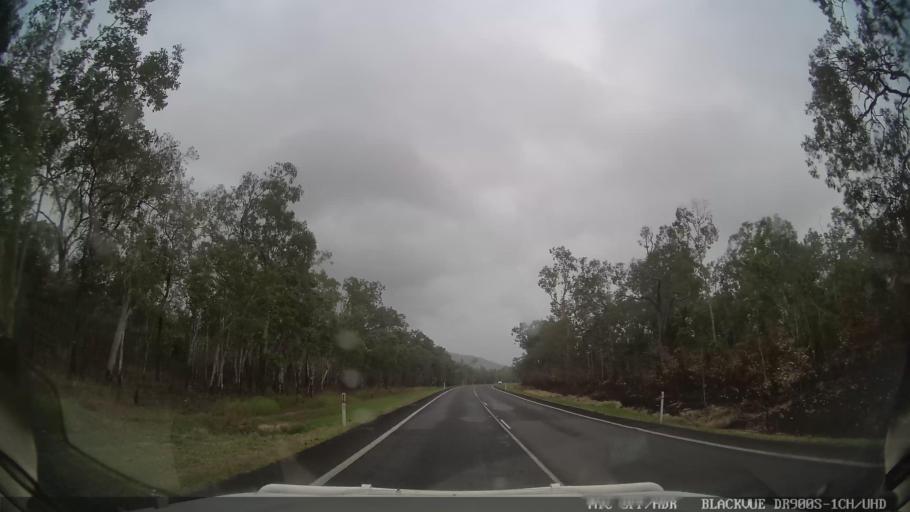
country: AU
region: Queensland
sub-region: Hinchinbrook
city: Ingham
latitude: -18.4400
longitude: 146.1395
